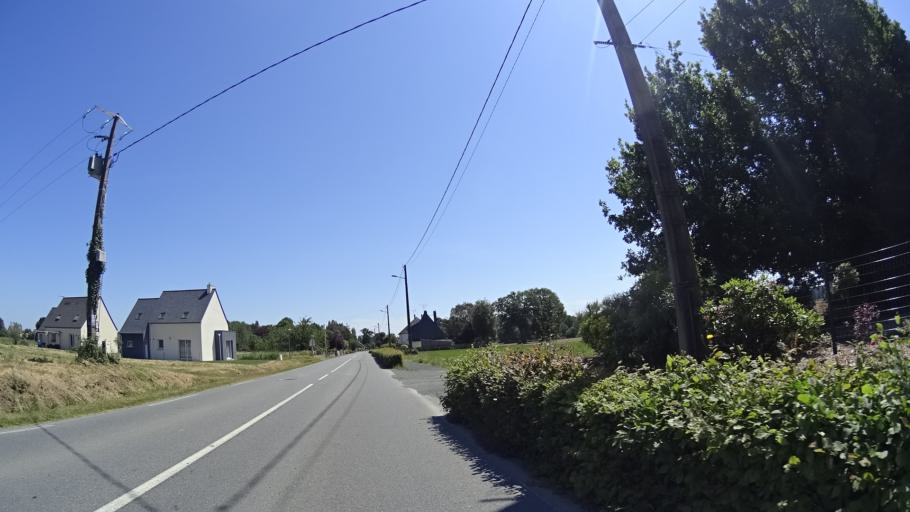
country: FR
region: Brittany
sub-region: Departement d'Ille-et-Vilaine
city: Messac
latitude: 47.8252
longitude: -1.7968
